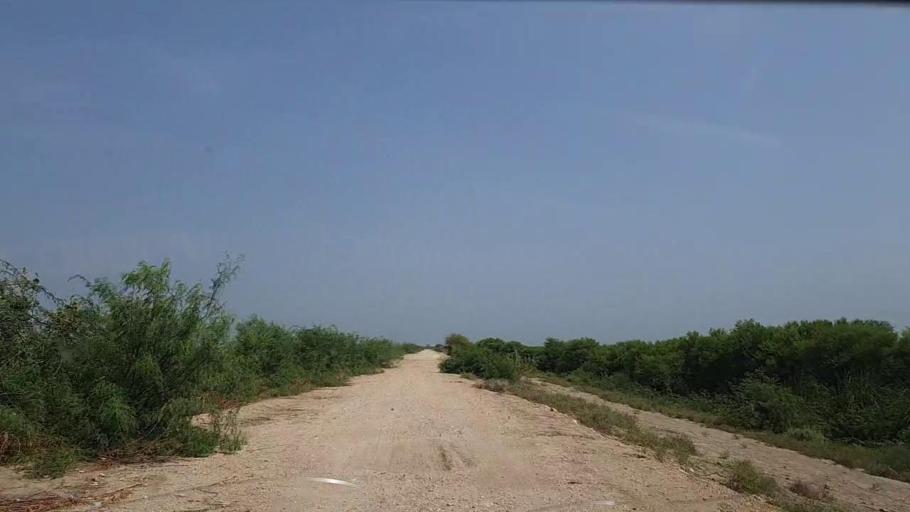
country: PK
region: Sindh
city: Ghotki
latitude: 28.1075
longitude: 69.3953
